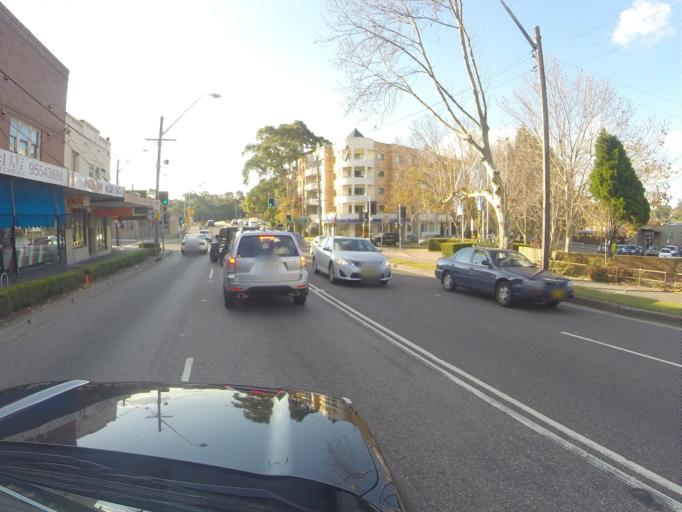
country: AU
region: New South Wales
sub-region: Rockdale
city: Bexley North
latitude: -33.9386
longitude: 151.1142
